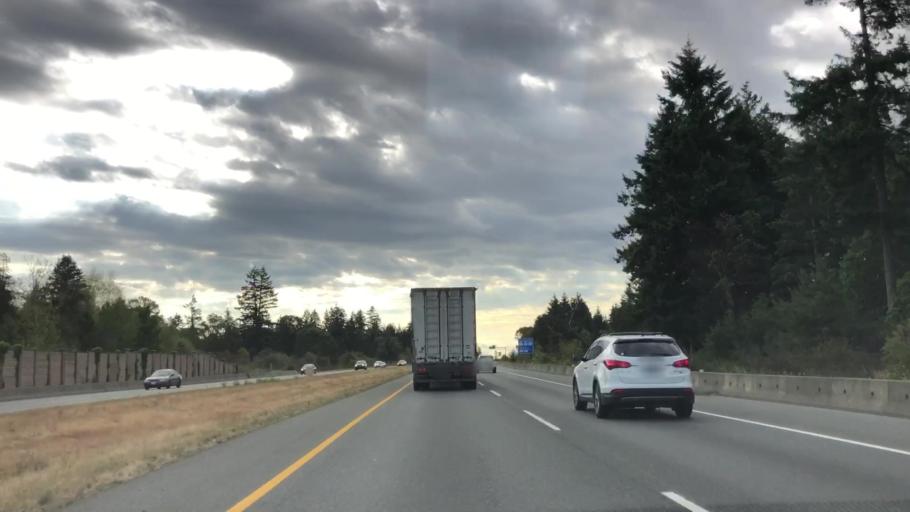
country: CA
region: British Columbia
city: Nanaimo
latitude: 49.1931
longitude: -124.0152
